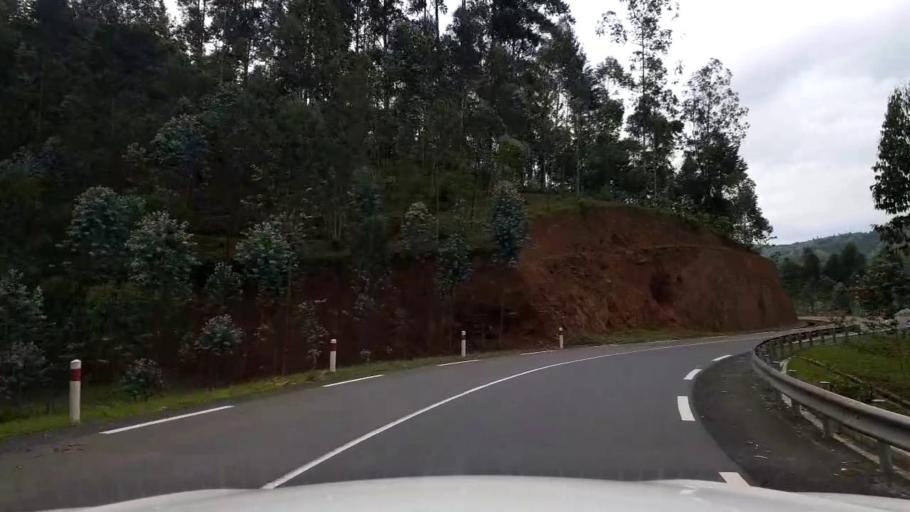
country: RW
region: Western Province
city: Kibuye
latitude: -1.9203
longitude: 29.3703
